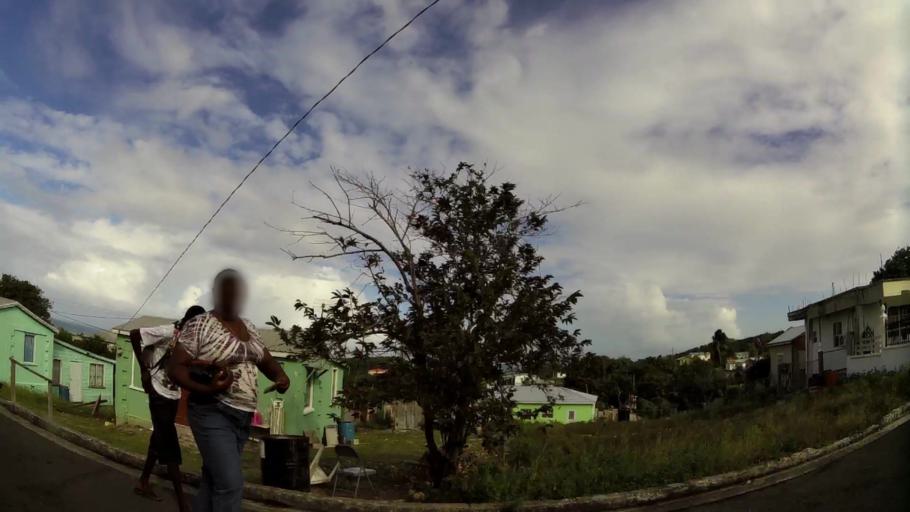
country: AG
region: Saint George
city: Piggotts
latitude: 17.1422
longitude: -61.8098
